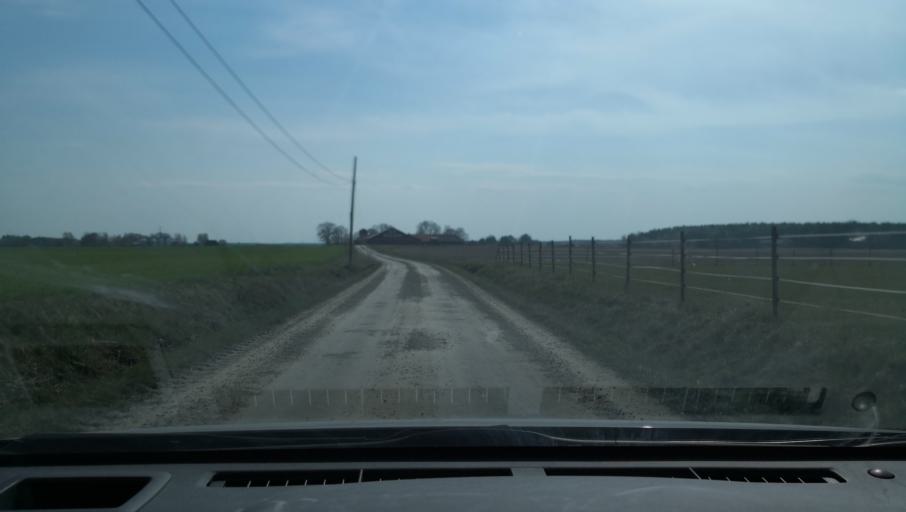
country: SE
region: Vaestmanland
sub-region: Vasteras
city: Skultuna
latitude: 59.8015
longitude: 16.4348
